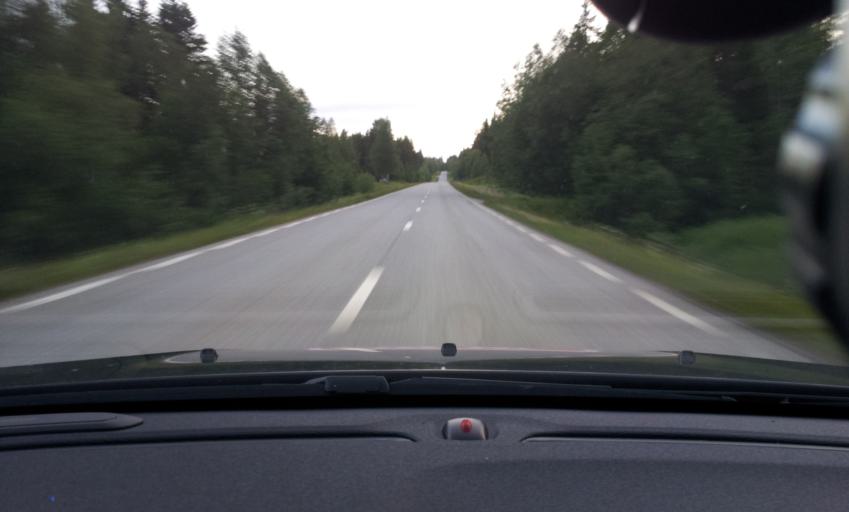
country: SE
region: Jaemtland
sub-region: Ragunda Kommun
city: Hammarstrand
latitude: 63.0269
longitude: 16.2990
